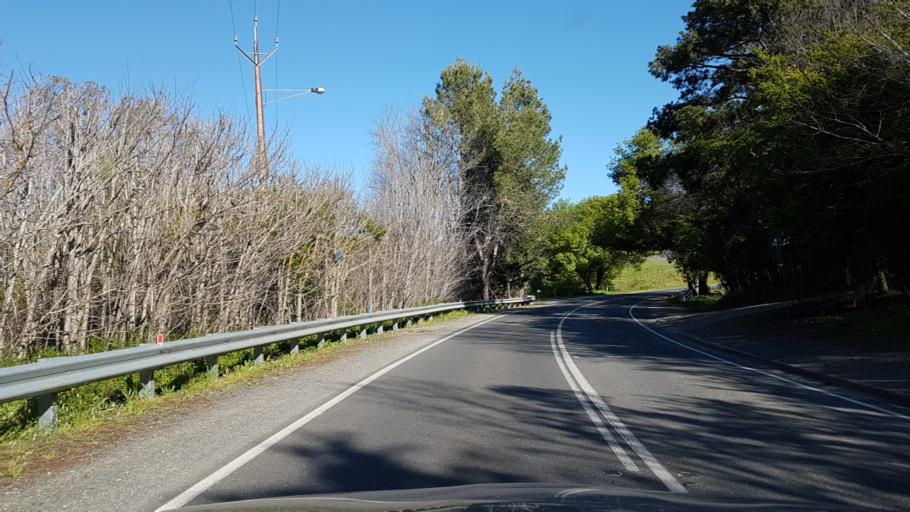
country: AU
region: South Australia
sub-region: Adelaide Hills
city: Gumeracha
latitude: -34.8297
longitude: 138.8906
